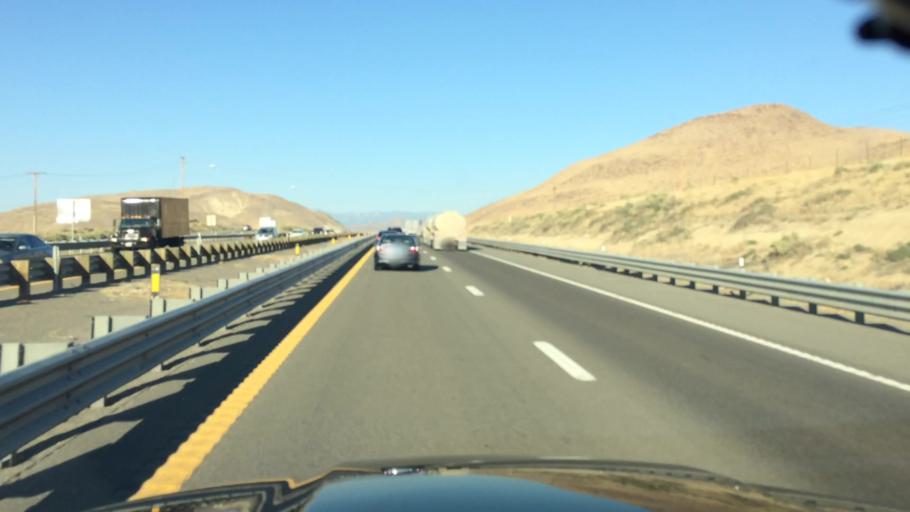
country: US
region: Nevada
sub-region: Washoe County
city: Spanish Springs
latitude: 39.5578
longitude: -119.5574
